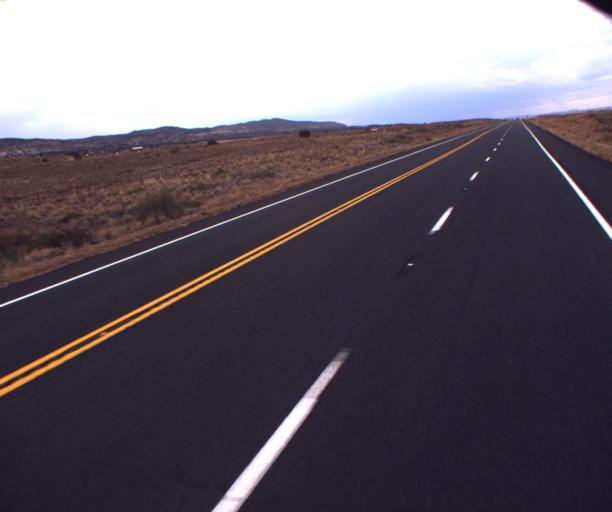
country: US
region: Arizona
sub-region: Coconino County
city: Kaibito
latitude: 36.4354
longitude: -110.7629
